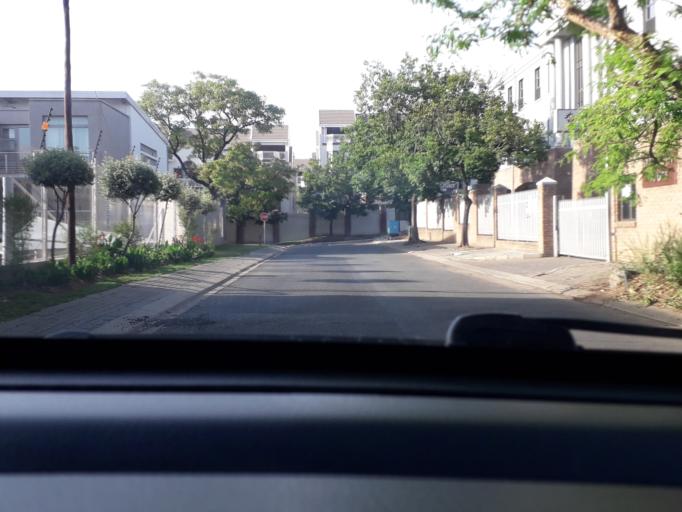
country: ZA
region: Gauteng
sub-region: City of Johannesburg Metropolitan Municipality
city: Midrand
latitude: -26.0609
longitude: 28.0619
